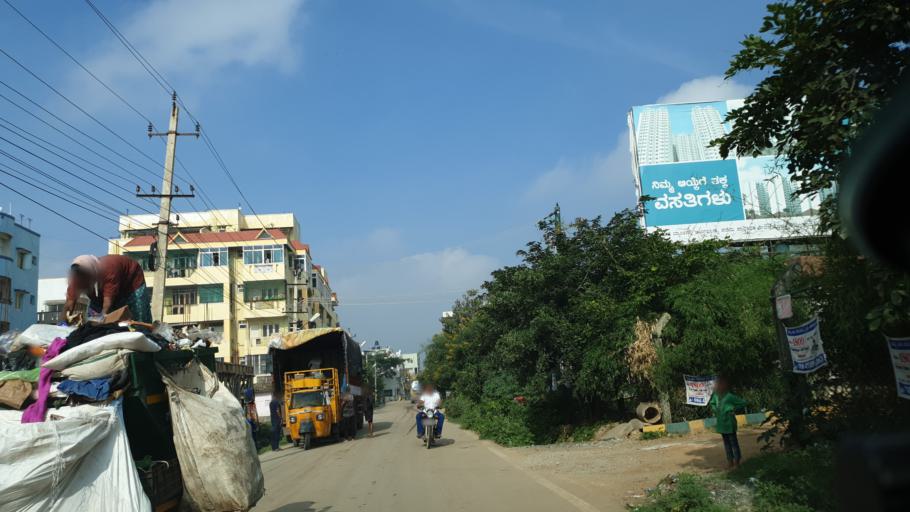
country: IN
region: Karnataka
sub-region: Bangalore Urban
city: Bangalore
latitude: 12.9714
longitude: 77.6918
